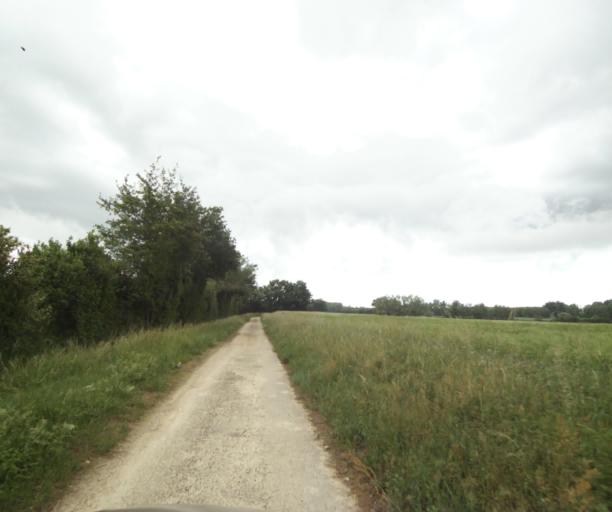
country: FR
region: Rhone-Alpes
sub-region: Departement de l'Ain
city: Tramoyes
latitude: 45.8570
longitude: 4.9539
